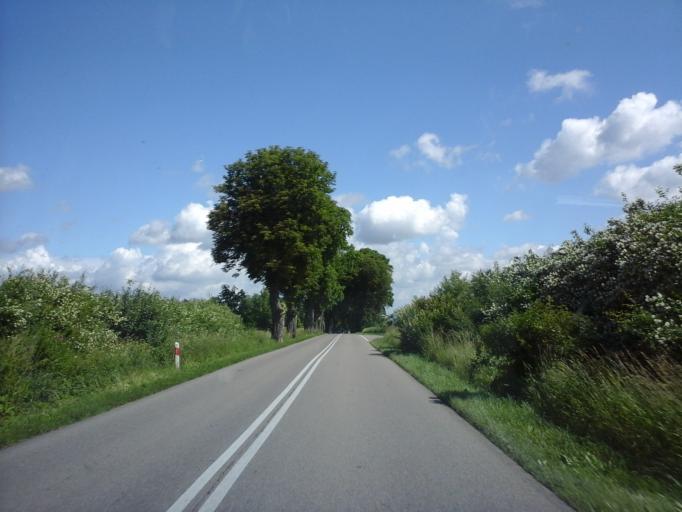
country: PL
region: West Pomeranian Voivodeship
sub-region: Powiat lobeski
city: Wegorzyno
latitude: 53.5795
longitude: 15.5909
